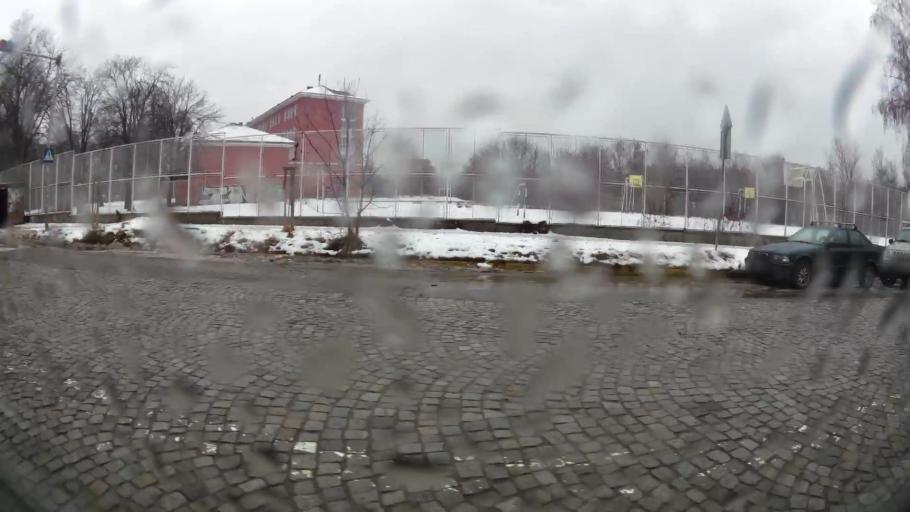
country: BG
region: Sofia-Capital
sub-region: Stolichna Obshtina
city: Sofia
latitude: 42.6727
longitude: 23.2621
